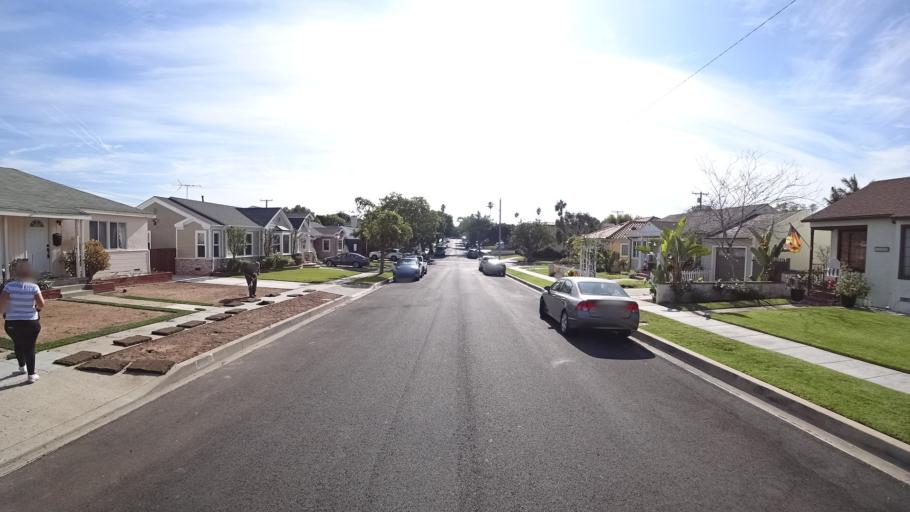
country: US
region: California
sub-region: Los Angeles County
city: Lawndale
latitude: 33.8898
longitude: -118.3801
